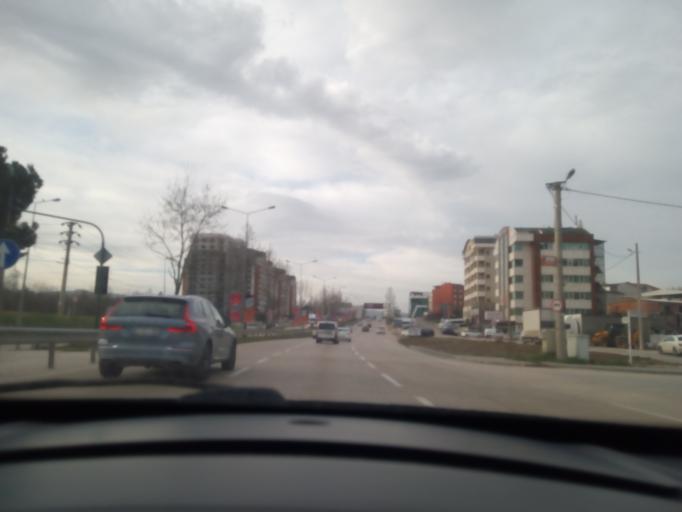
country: TR
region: Bursa
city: Niluefer
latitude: 40.2286
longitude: 28.9633
